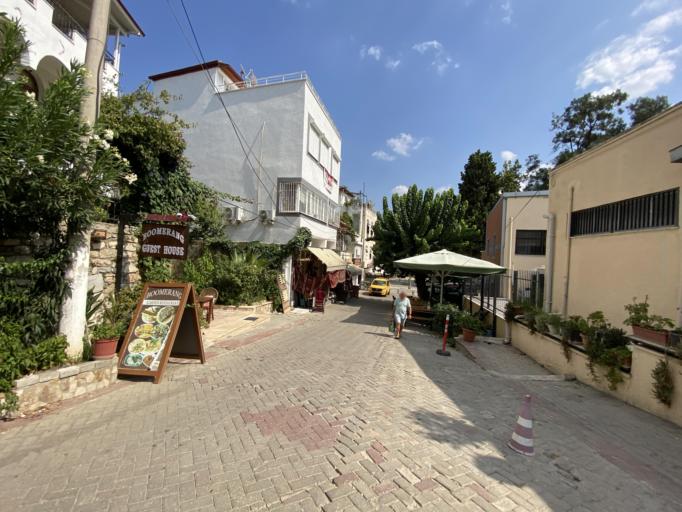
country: TR
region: Izmir
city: Selcuk
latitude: 37.9493
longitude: 27.3678
